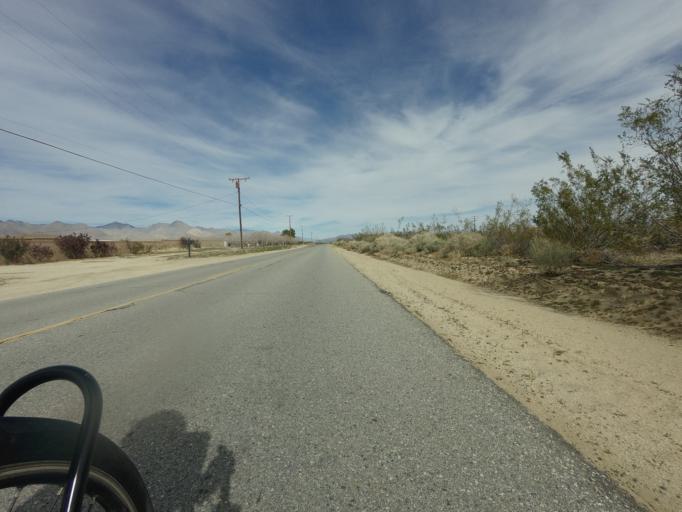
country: US
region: California
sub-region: Kern County
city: Inyokern
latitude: 35.7039
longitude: -117.8292
